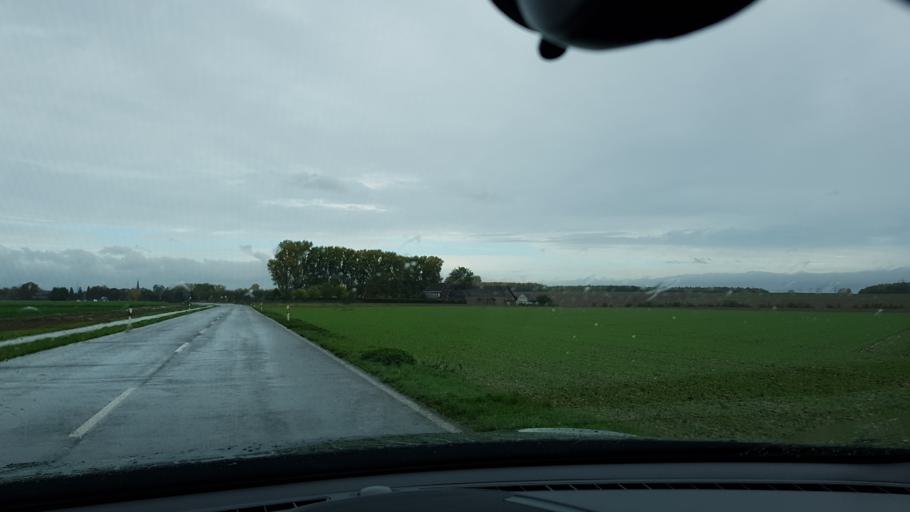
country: DE
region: North Rhine-Westphalia
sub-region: Regierungsbezirk Dusseldorf
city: Rommerskirchen
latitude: 51.0654
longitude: 6.7054
